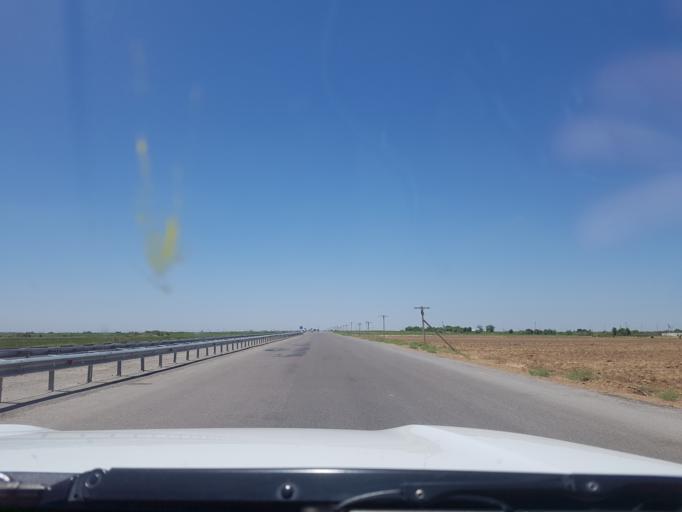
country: TM
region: Mary
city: Mary
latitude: 37.2618
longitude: 61.2681
